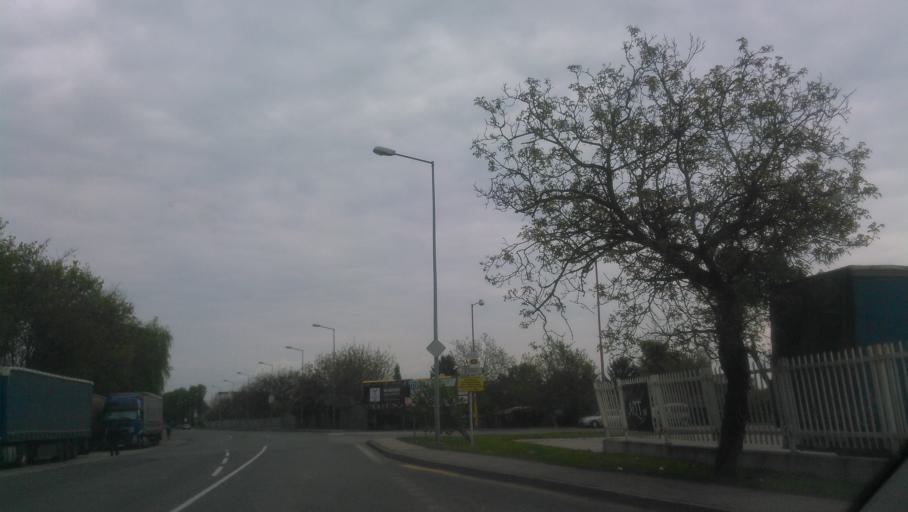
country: SK
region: Bratislavsky
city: Bratislava
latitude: 48.1293
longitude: 17.1797
